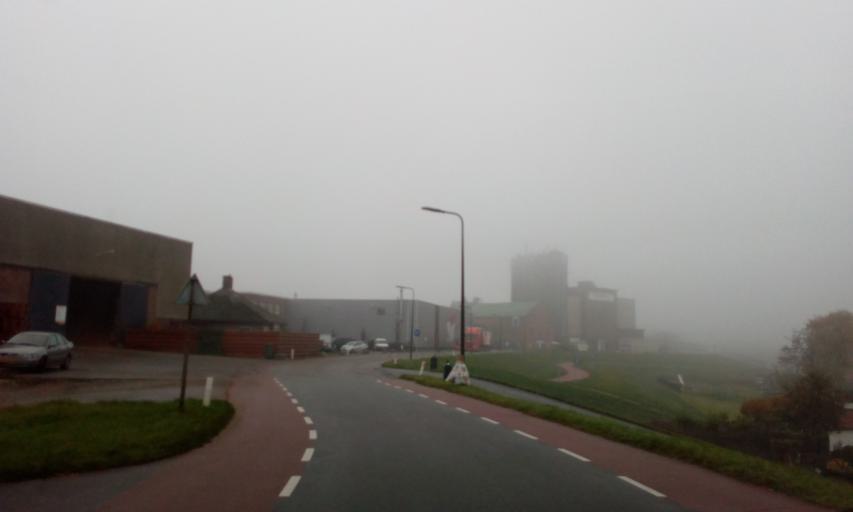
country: NL
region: South Holland
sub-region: Molenwaard
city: Liesveld
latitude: 51.9226
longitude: 4.7878
